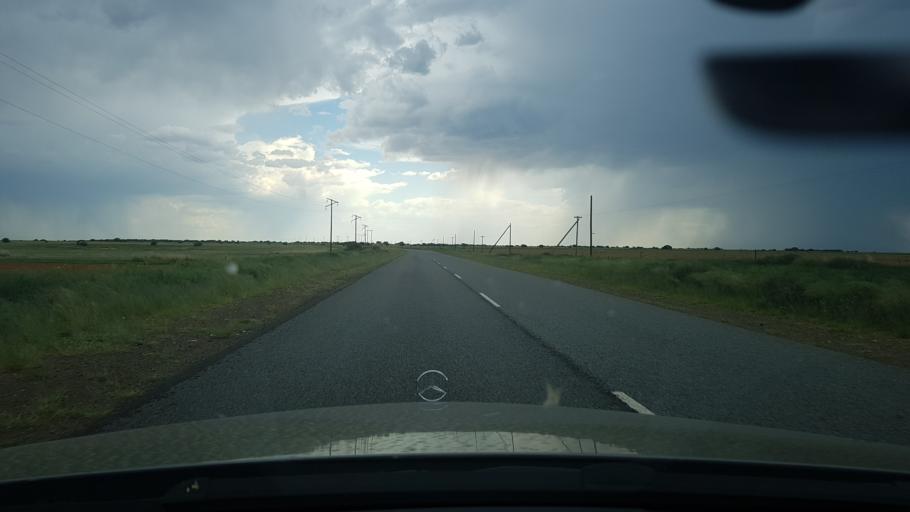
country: ZA
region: Orange Free State
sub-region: Lejweleputswa District Municipality
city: Hoopstad
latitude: -28.0293
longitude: 25.5921
